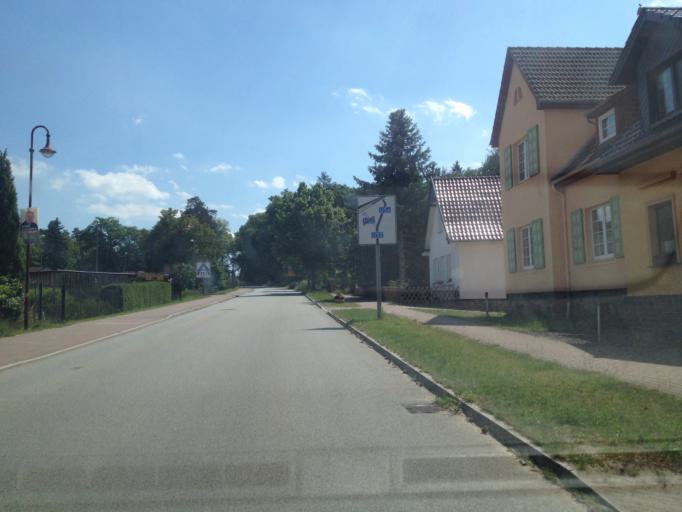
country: DE
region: Brandenburg
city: Joachimsthal
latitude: 52.9750
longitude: 13.7545
